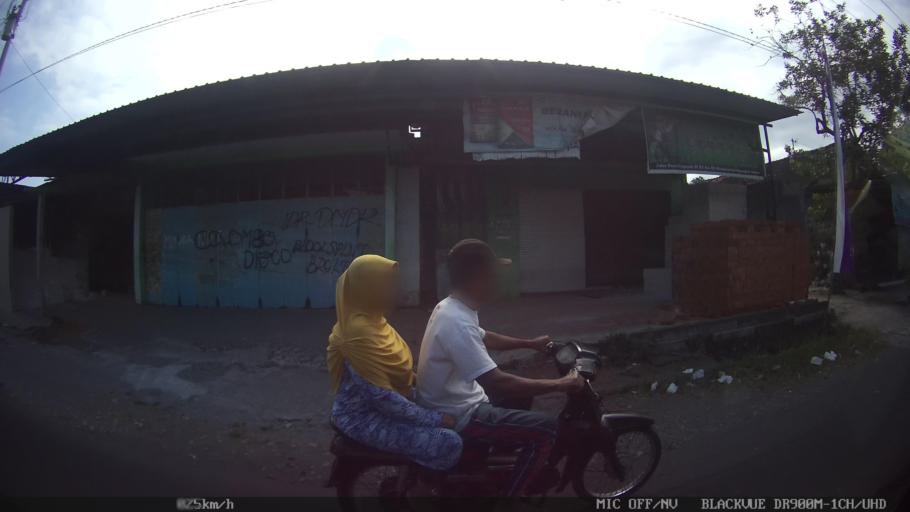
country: ID
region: Daerah Istimewa Yogyakarta
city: Depok
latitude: -7.7283
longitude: 110.4143
